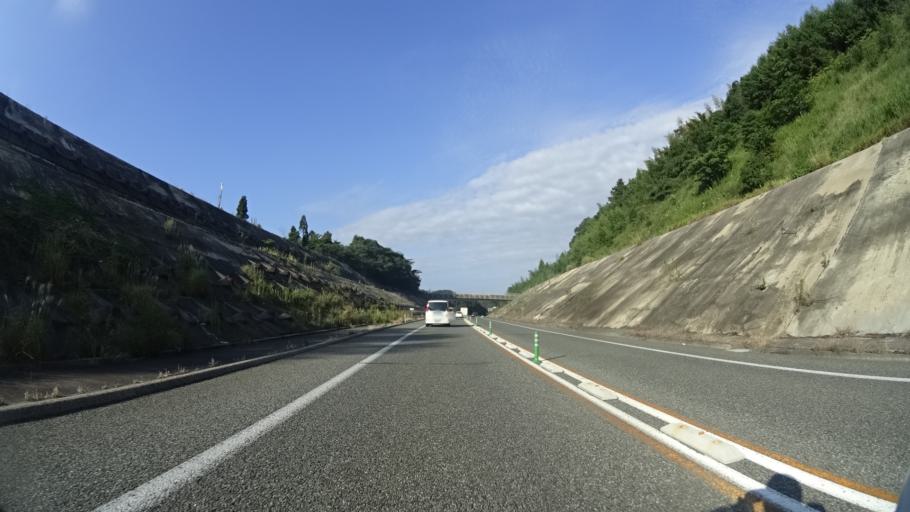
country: JP
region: Shimane
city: Hiratacho
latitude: 35.3981
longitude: 132.9219
